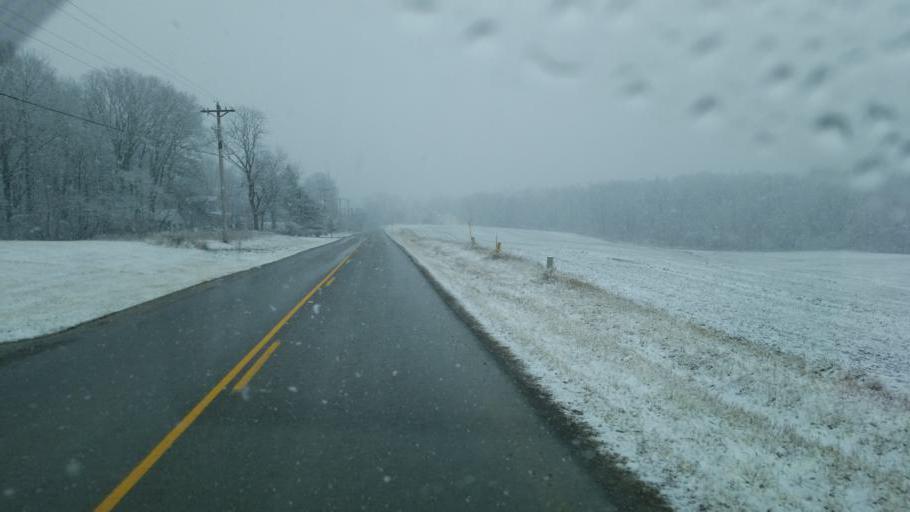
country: US
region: Ohio
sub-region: Champaign County
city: North Lewisburg
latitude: 40.3359
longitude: -83.5968
